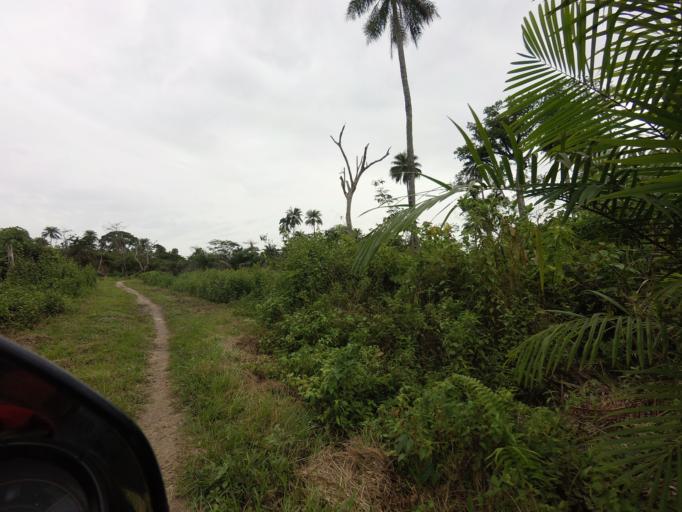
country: SL
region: Eastern Province
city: Mobai
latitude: 7.9807
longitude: -10.7092
